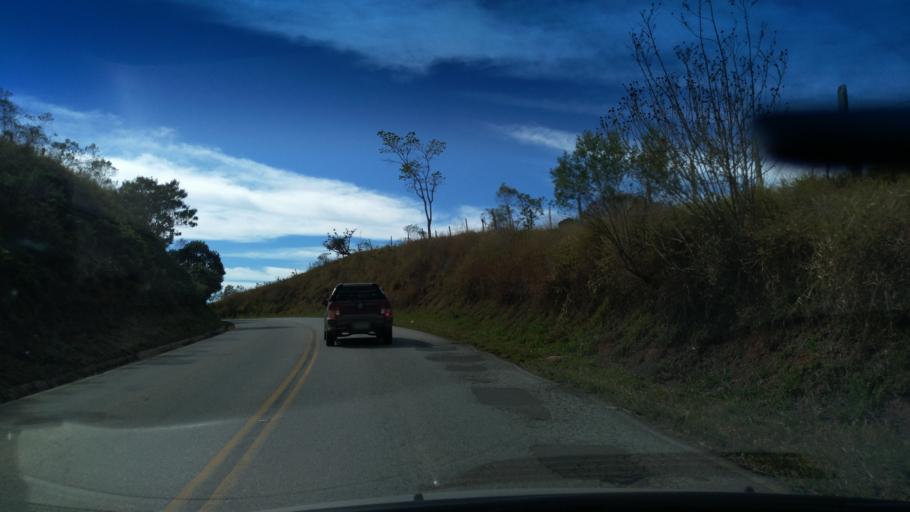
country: BR
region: Minas Gerais
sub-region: Andradas
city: Andradas
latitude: -22.0690
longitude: -46.4426
